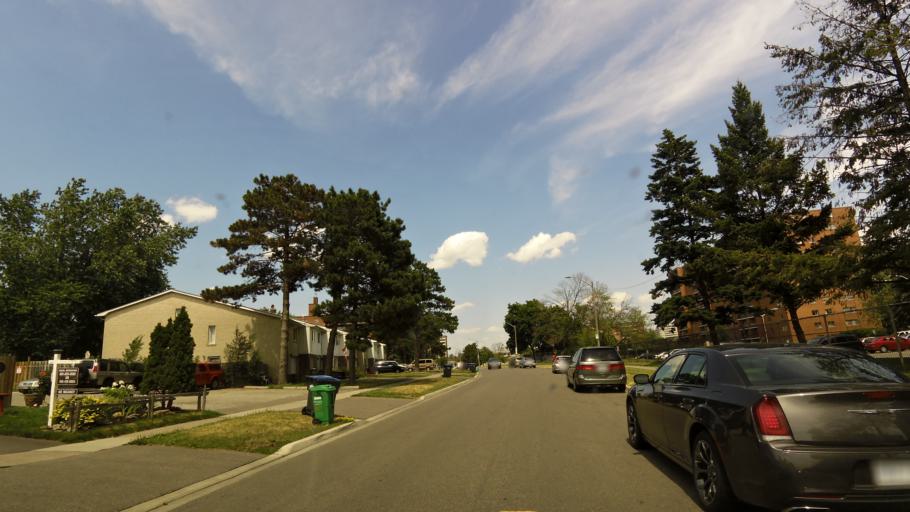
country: CA
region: Ontario
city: Etobicoke
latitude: 43.6220
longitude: -79.5907
